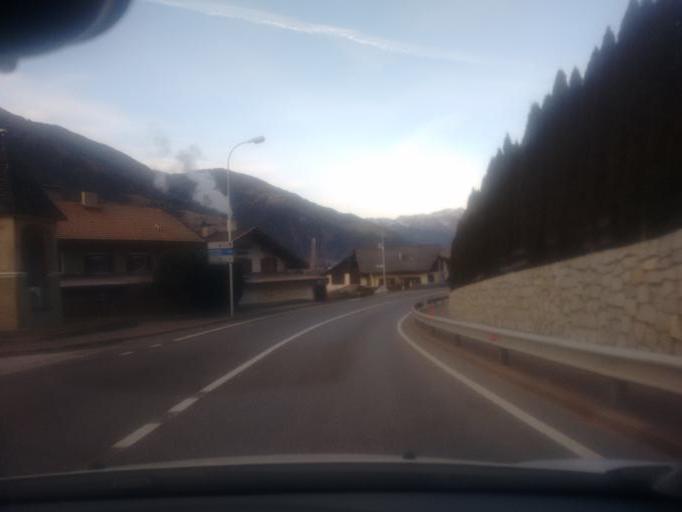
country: IT
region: Trentino-Alto Adige
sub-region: Bolzano
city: Campo di Trens
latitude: 46.8718
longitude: 11.4843
